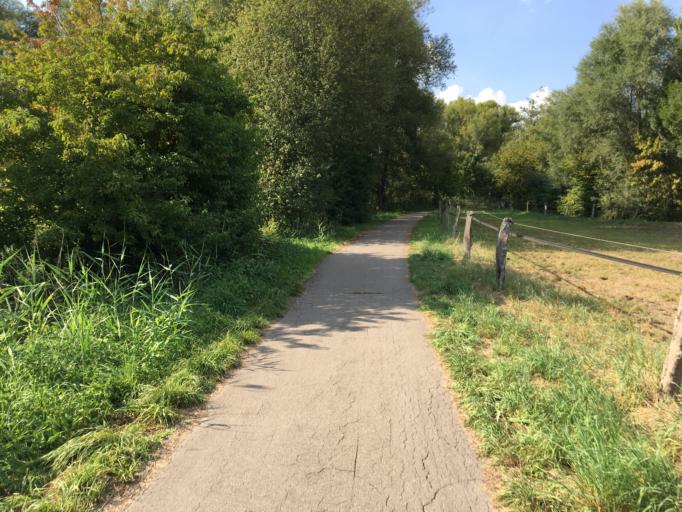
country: DE
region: Lower Saxony
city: Leiferde
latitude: 52.2139
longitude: 10.5090
